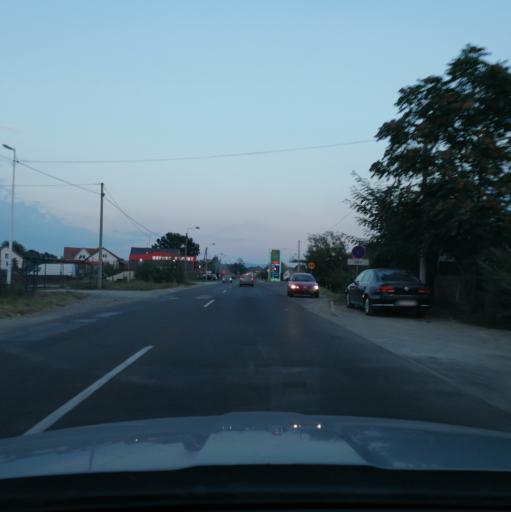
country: RS
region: Central Serbia
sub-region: Raski Okrug
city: Kraljevo
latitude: 43.7030
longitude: 20.7240
